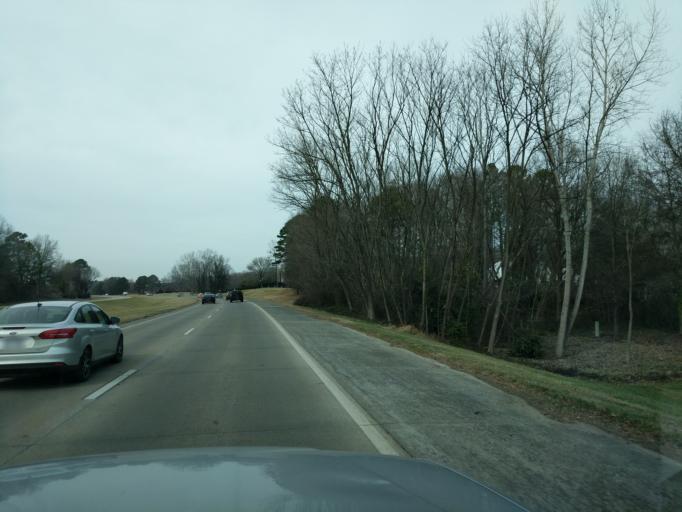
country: US
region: North Carolina
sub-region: Mecklenburg County
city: Charlotte
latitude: 35.1840
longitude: -80.8957
